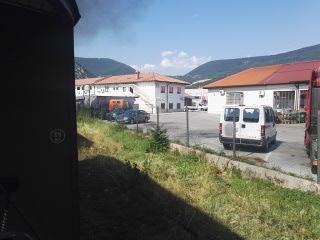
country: SI
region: Nova Gorica
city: Solkan
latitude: 45.9679
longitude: 13.6400
